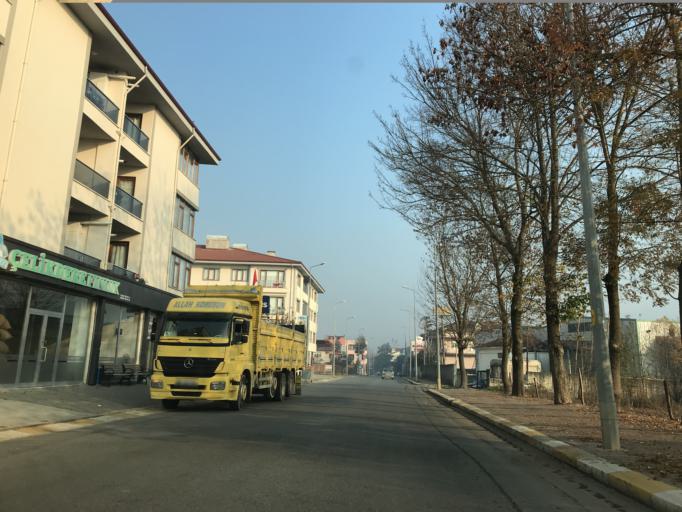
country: TR
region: Duzce
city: Cumayeri
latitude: 40.8796
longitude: 30.9508
